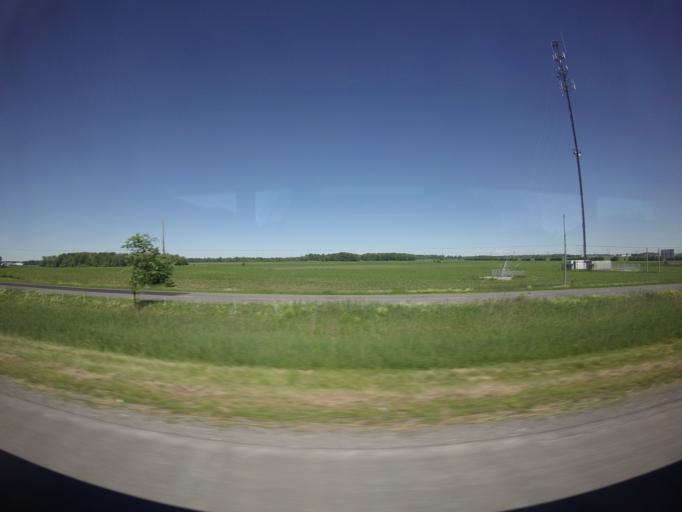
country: CA
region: Quebec
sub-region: Monteregie
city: Acton Vale
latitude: 45.7411
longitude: -72.7283
